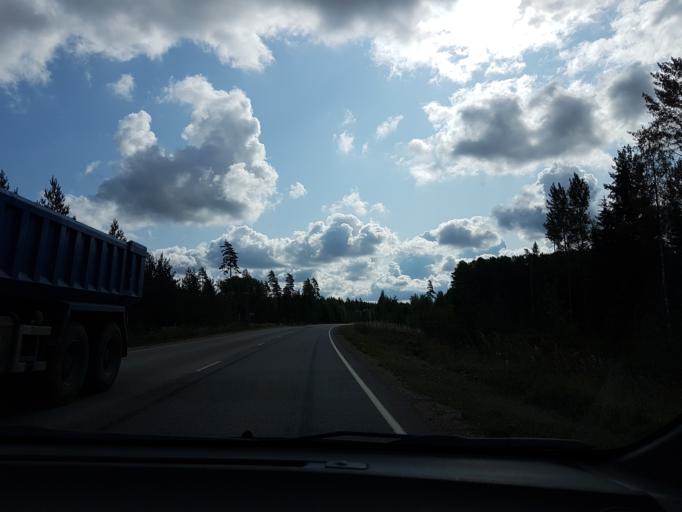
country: FI
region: Uusimaa
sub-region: Helsinki
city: Nickby
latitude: 60.4701
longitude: 25.2677
